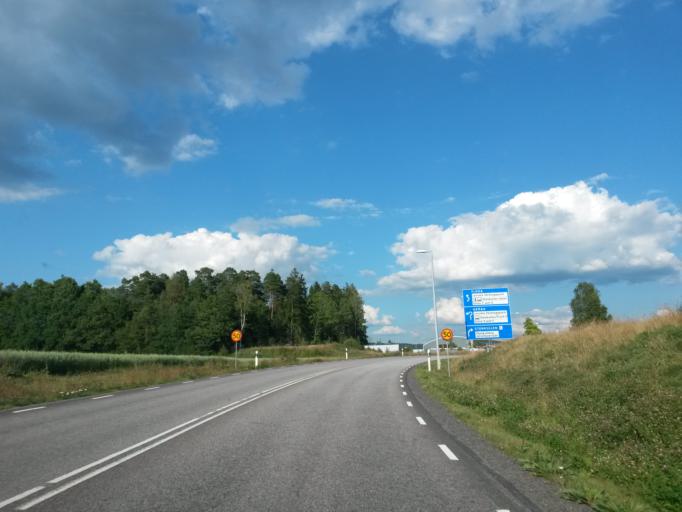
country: SE
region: Vaestra Goetaland
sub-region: Lerums Kommun
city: Stenkullen
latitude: 57.7961
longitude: 12.3046
